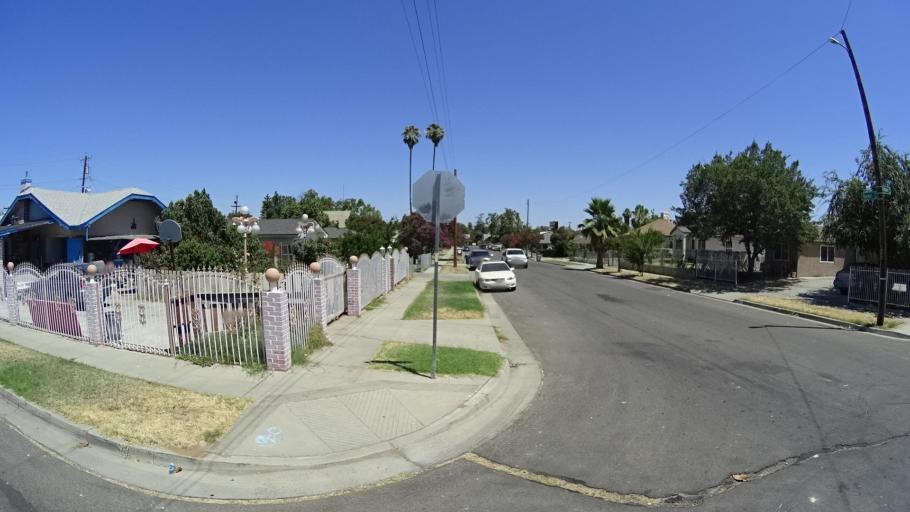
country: US
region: California
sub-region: Fresno County
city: Fresno
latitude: 36.7413
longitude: -119.7437
